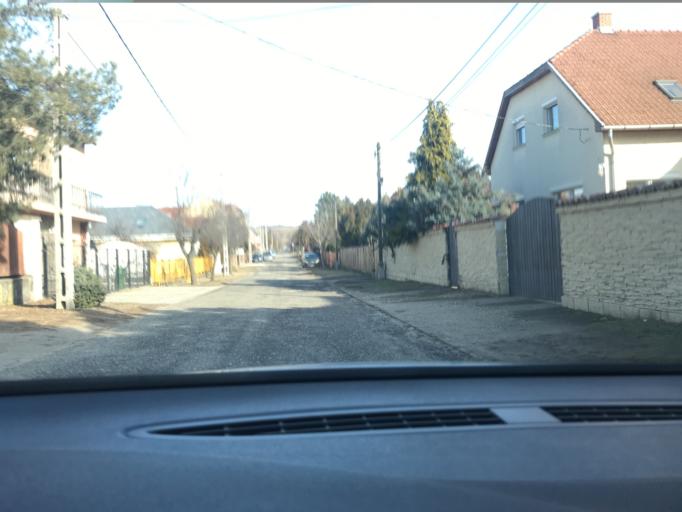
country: HU
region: Pest
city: Fot
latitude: 47.6287
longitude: 19.1764
